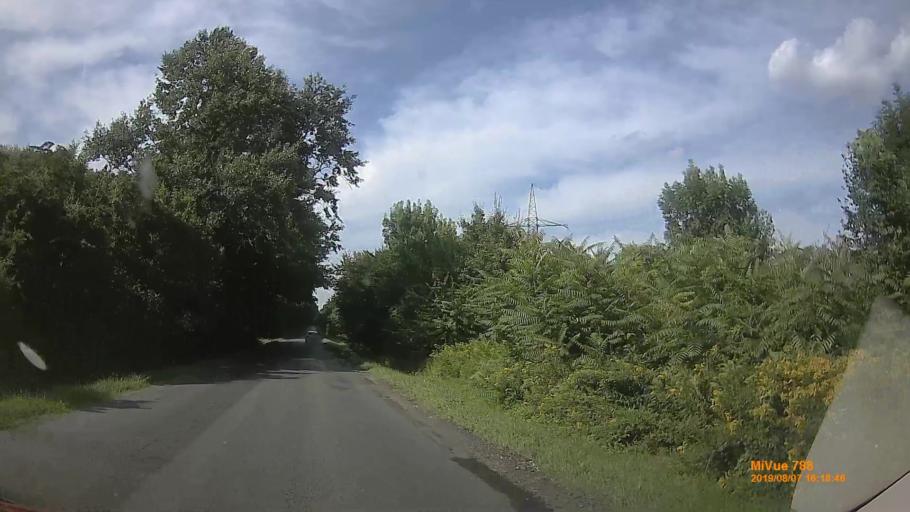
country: HU
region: Zala
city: Cserszegtomaj
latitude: 46.8431
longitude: 17.2676
